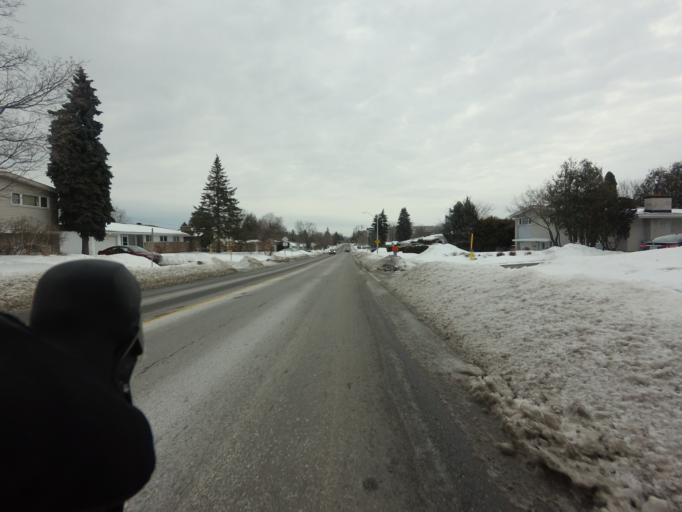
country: CA
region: Ontario
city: Ottawa
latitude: 45.3583
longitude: -75.7254
